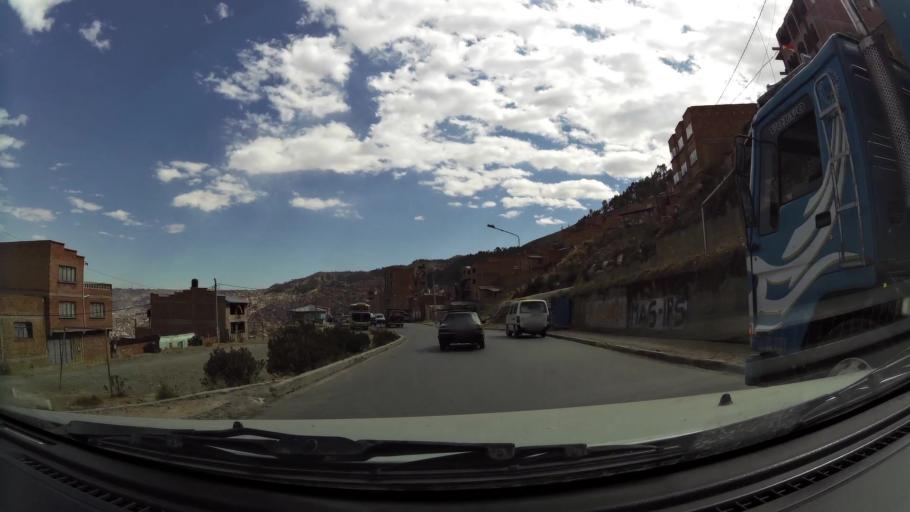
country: BO
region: La Paz
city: La Paz
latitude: -16.4641
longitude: -68.1126
